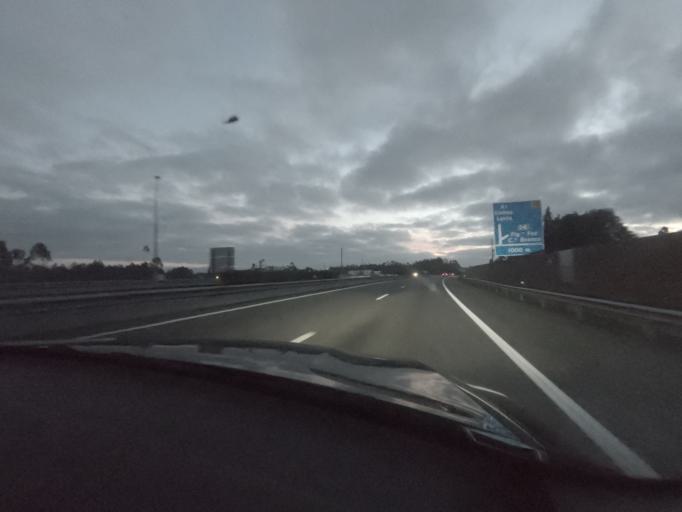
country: PT
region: Leiria
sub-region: Pombal
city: Pombal
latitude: 39.9465
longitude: -8.6719
